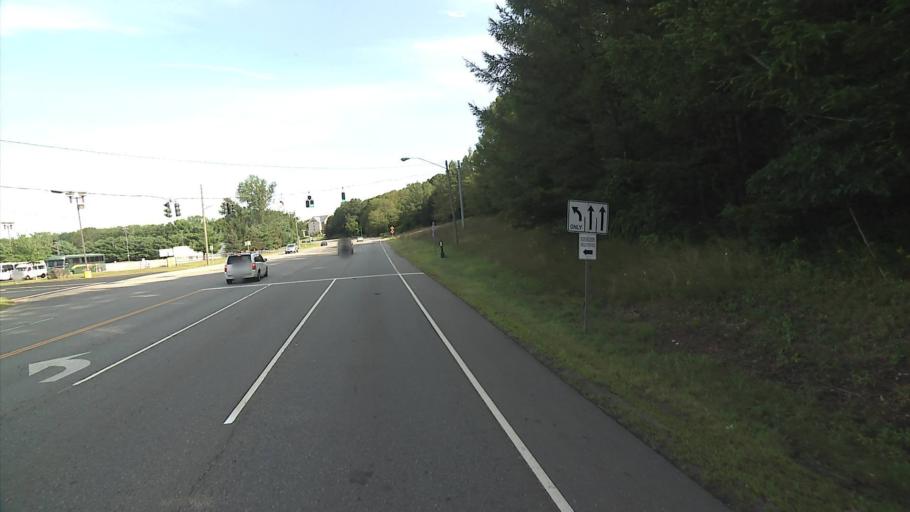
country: US
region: Connecticut
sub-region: New London County
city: Preston City
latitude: 41.4845
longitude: -71.9696
